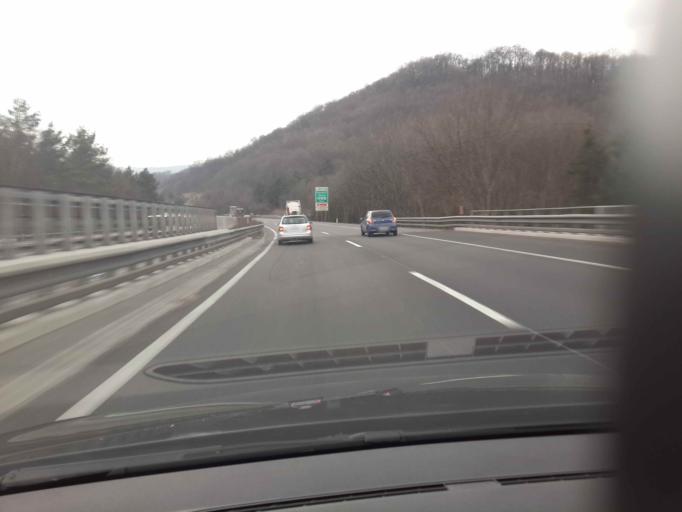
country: AT
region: Lower Austria
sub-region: Politischer Bezirk Baden
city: Alland
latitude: 48.0602
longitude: 16.0942
